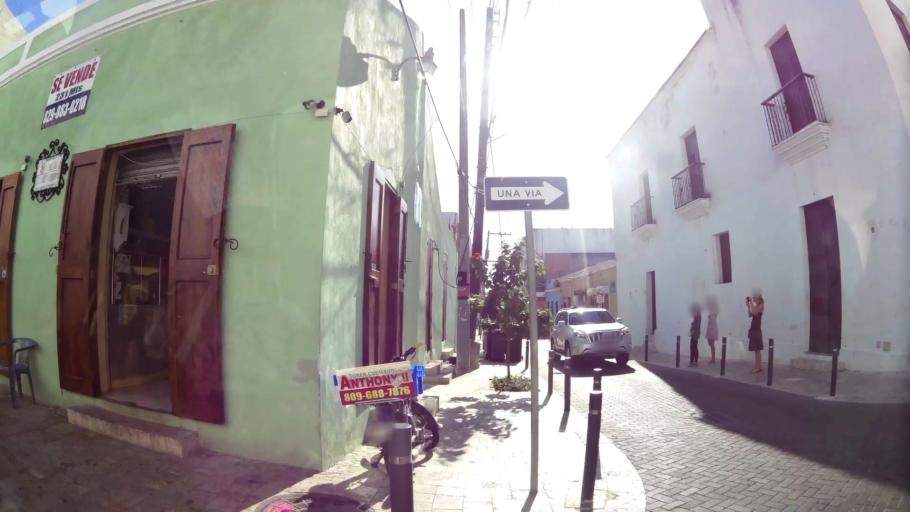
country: DO
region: Nacional
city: San Carlos
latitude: 18.4773
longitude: -69.8850
